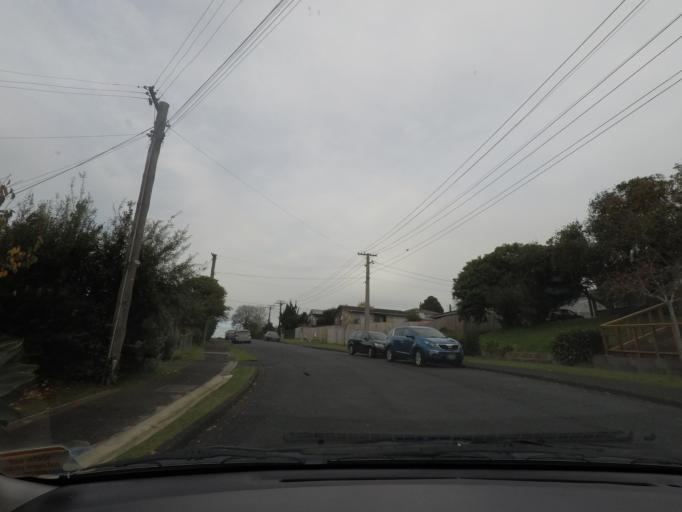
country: NZ
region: Auckland
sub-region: Auckland
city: Rosebank
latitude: -36.8589
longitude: 174.6403
